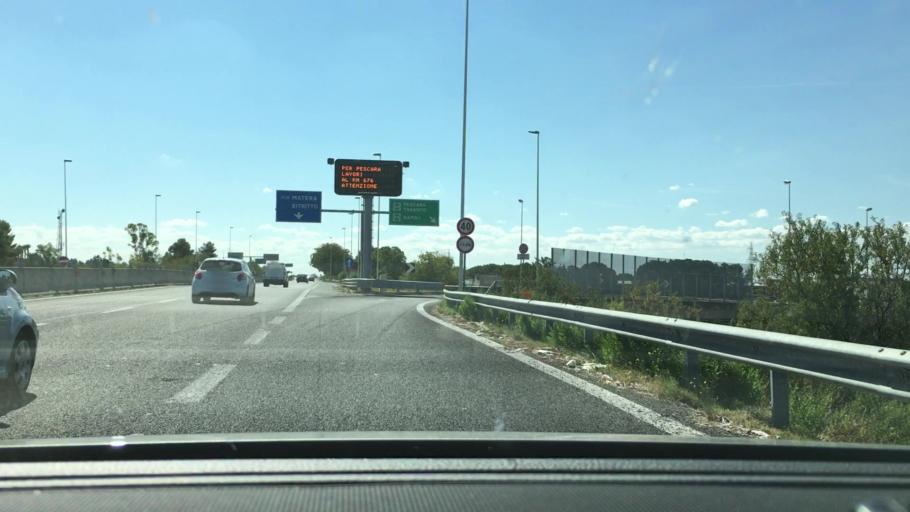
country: IT
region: Apulia
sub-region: Provincia di Bari
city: Bitritto
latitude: 41.0727
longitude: 16.8294
